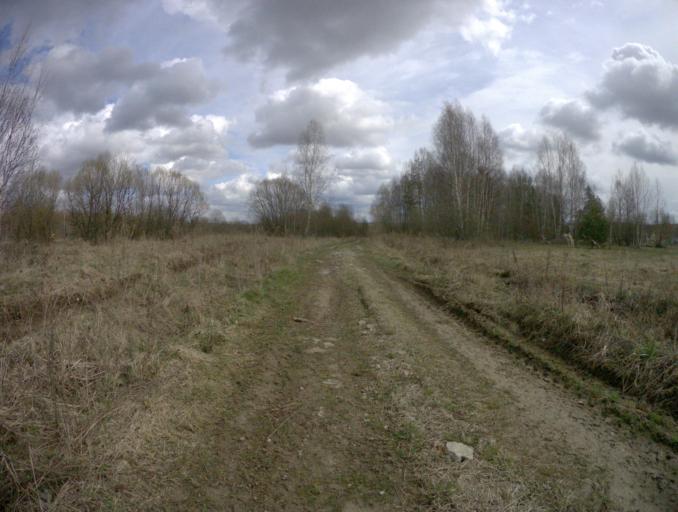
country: RU
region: Vladimir
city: Orgtrud
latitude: 56.0749
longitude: 40.7378
